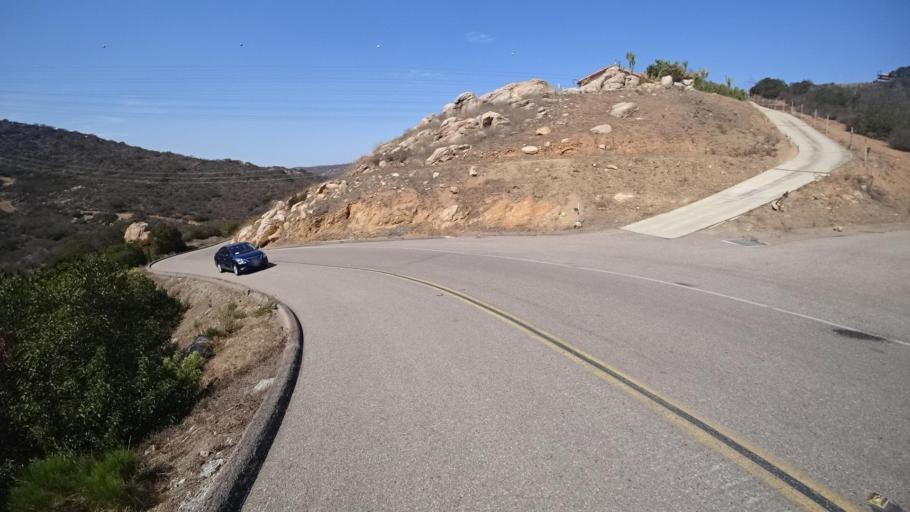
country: US
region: California
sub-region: San Diego County
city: Rancho San Diego
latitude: 32.7211
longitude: -116.9295
